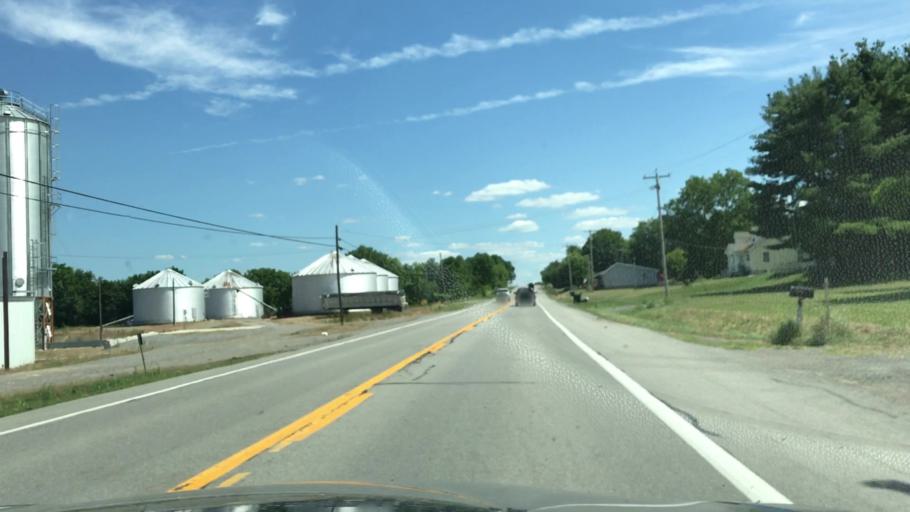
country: US
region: New York
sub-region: Livingston County
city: Mount Morris
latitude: 42.6778
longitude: -77.8180
